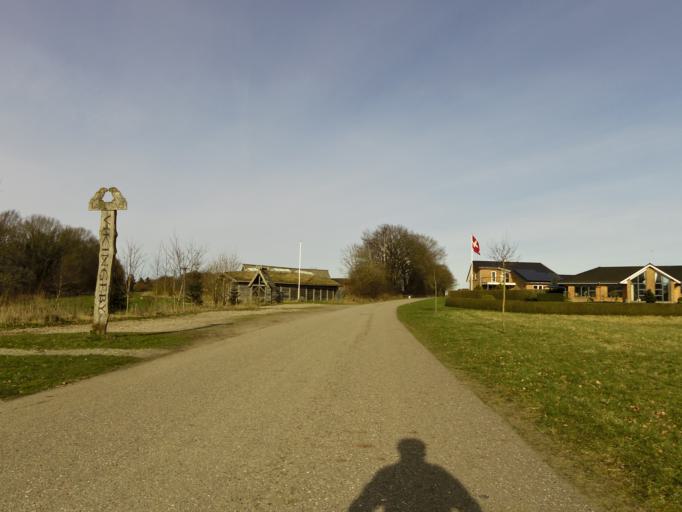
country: DK
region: South Denmark
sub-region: Kolding Kommune
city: Vamdrup
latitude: 55.3610
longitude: 9.2203
